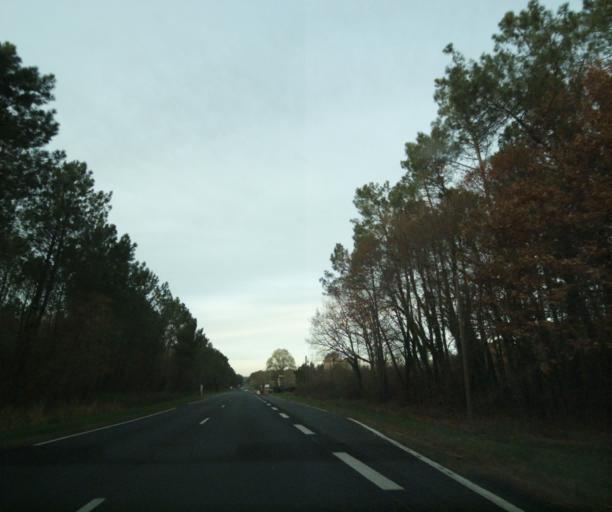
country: FR
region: Aquitaine
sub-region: Departement de la Gironde
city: Bazas
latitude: 44.3439
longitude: -0.2355
